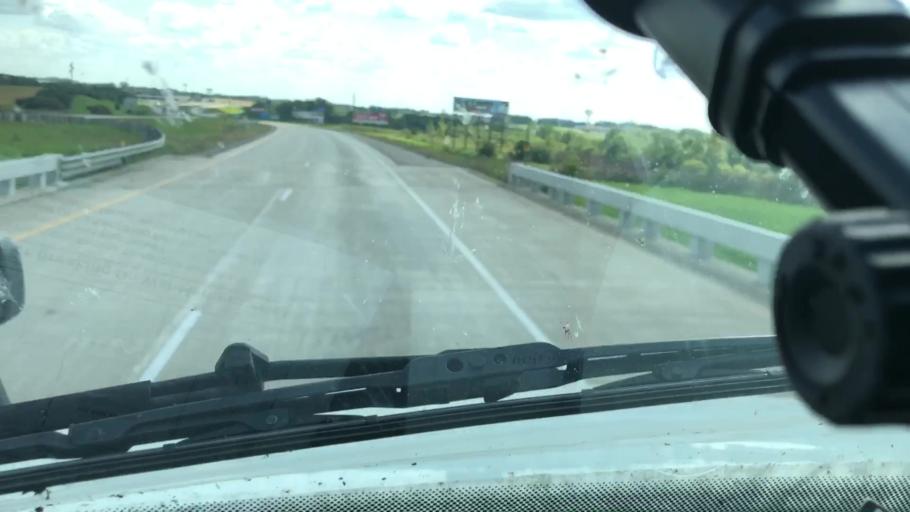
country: US
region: Minnesota
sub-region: Freeborn County
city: Albert Lea
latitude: 43.6690
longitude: -93.3234
